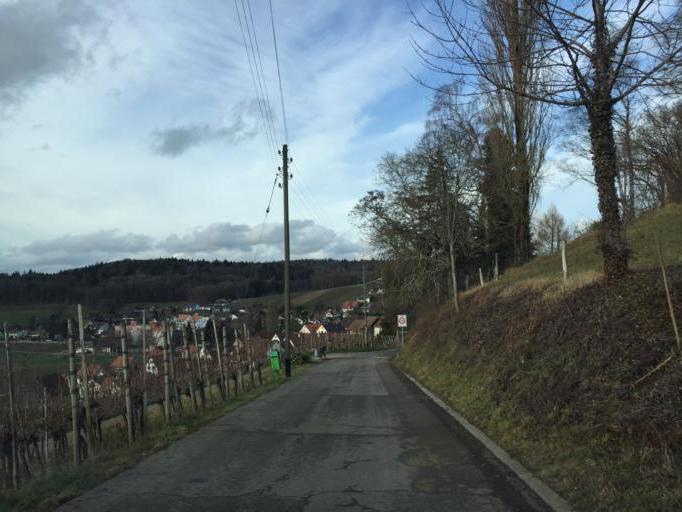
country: CH
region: Zurich
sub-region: Bezirk Andelfingen
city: Kleinandelfingen
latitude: 47.6344
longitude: 8.6936
